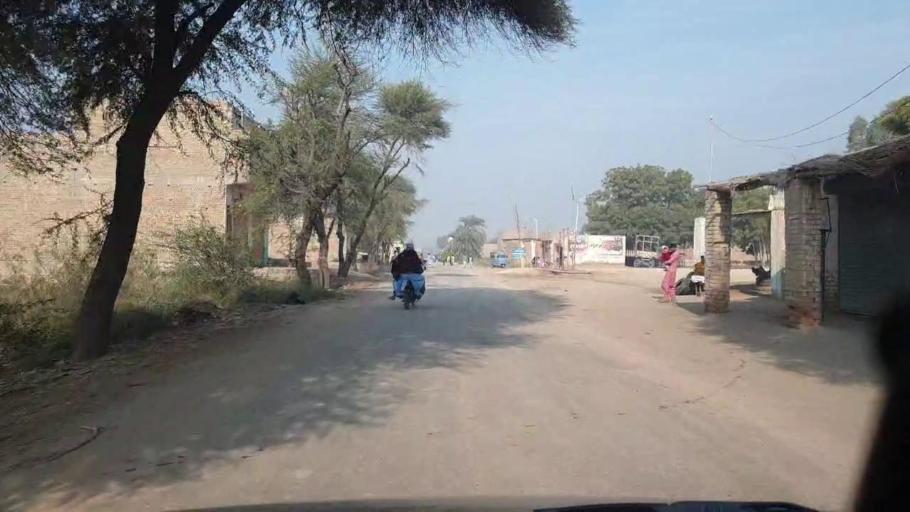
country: PK
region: Sindh
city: Shahdadpur
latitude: 25.9315
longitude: 68.6126
